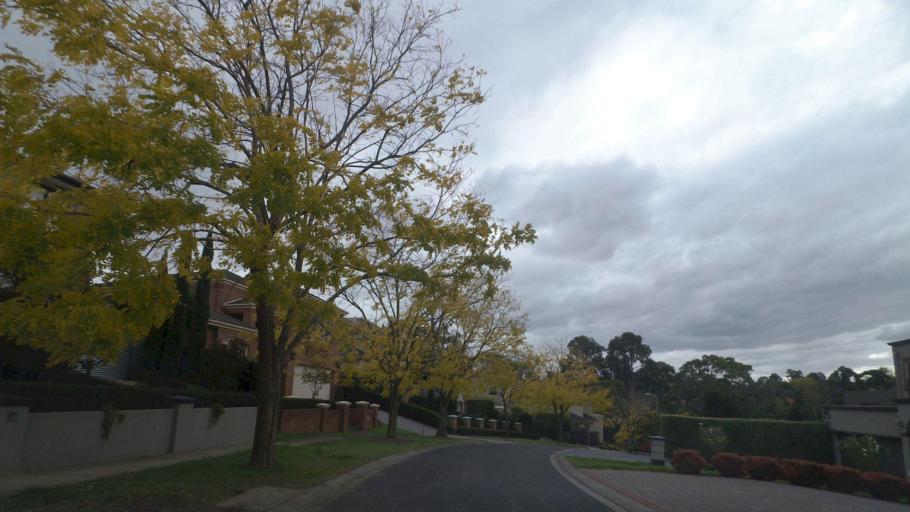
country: AU
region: Victoria
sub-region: Nillumbik
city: Eltham
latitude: -37.7572
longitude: 145.1614
